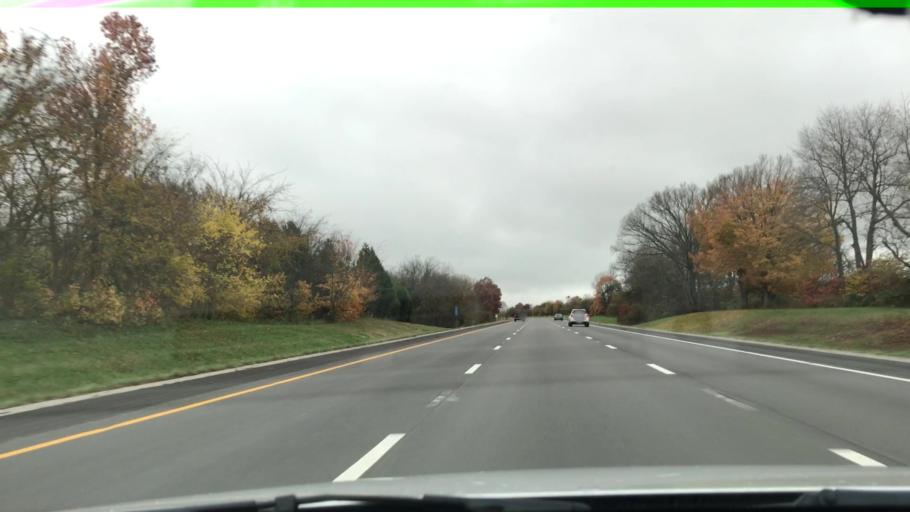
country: US
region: Kentucky
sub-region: Edmonson County
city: Brownsville
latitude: 37.0183
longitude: -86.2687
